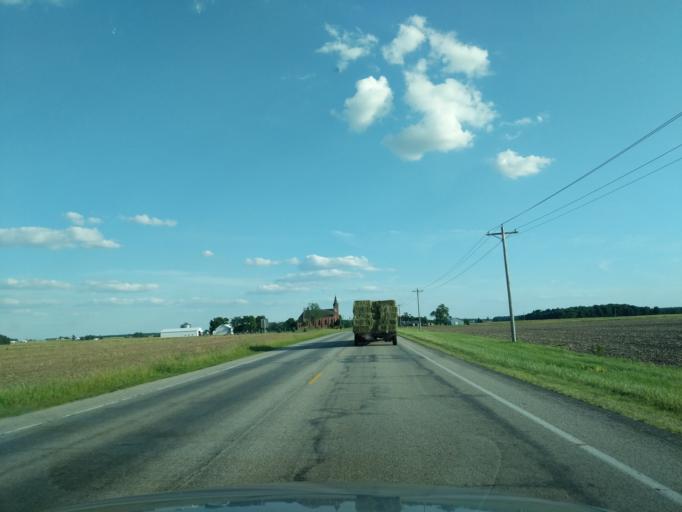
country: US
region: Indiana
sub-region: Huntington County
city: Roanoke
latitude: 41.0228
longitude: -85.4707
